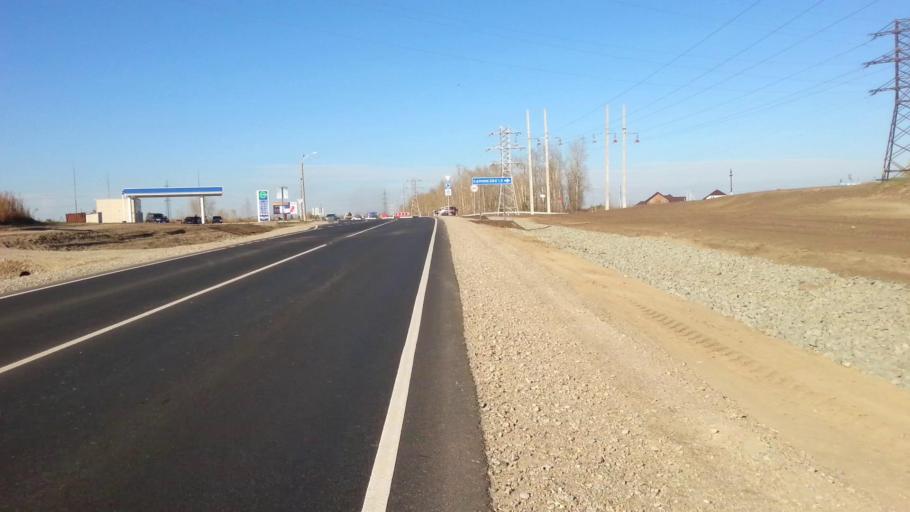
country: RU
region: Altai Krai
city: Sannikovo
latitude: 53.3357
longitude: 83.9385
